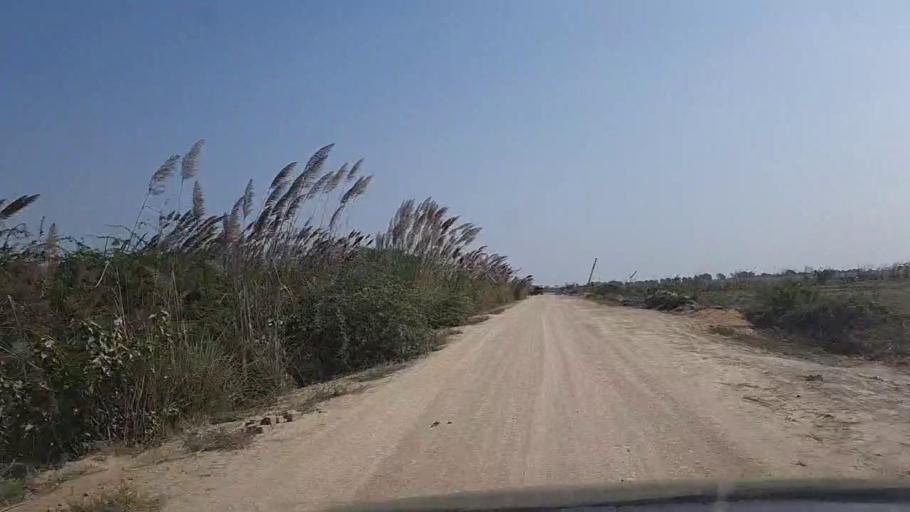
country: PK
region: Sindh
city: Gharo
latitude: 24.7188
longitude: 67.5624
